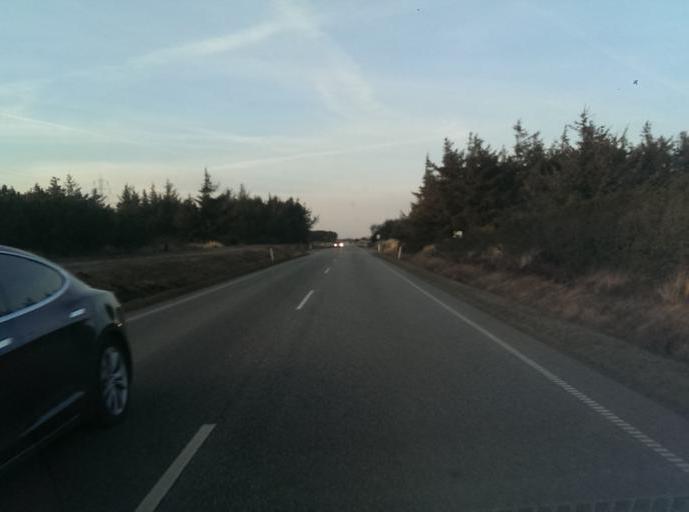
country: DK
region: Central Jutland
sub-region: Ringkobing-Skjern Kommune
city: Hvide Sande
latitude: 56.0880
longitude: 8.1222
